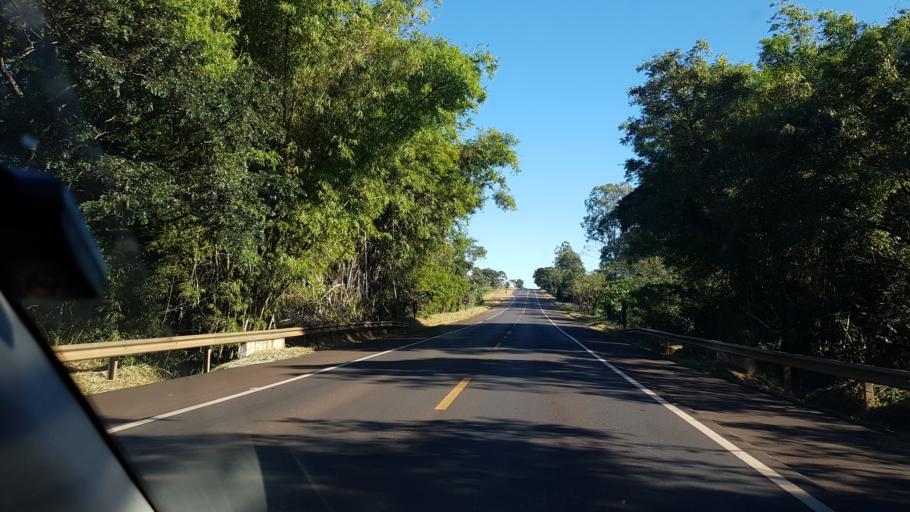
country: BR
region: Sao Paulo
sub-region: Assis
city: Assis
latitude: -22.5803
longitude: -50.5068
